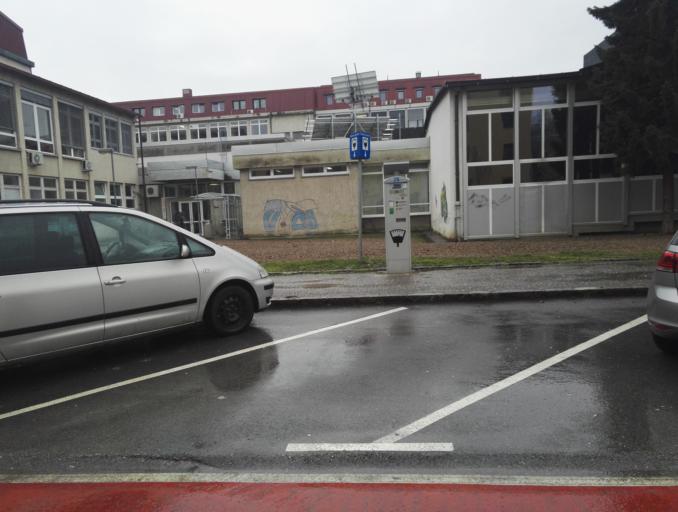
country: SI
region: Maribor
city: Maribor
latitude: 46.5597
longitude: 15.6389
